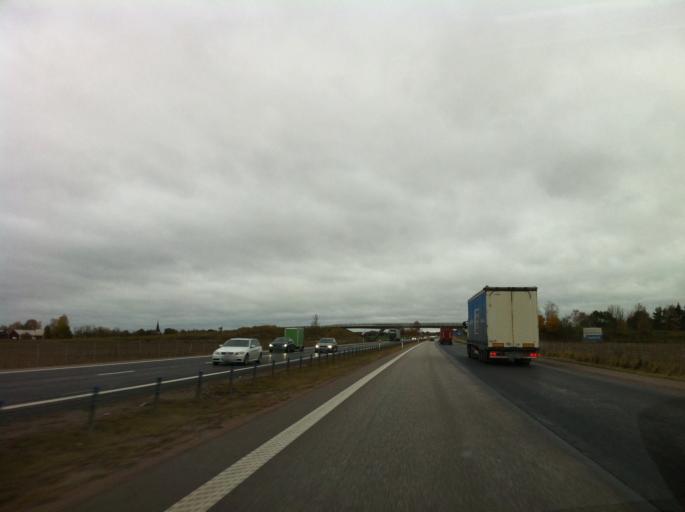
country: SE
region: OEstergoetland
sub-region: Mjolby Kommun
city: Mantorp
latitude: 58.3770
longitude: 15.3318
